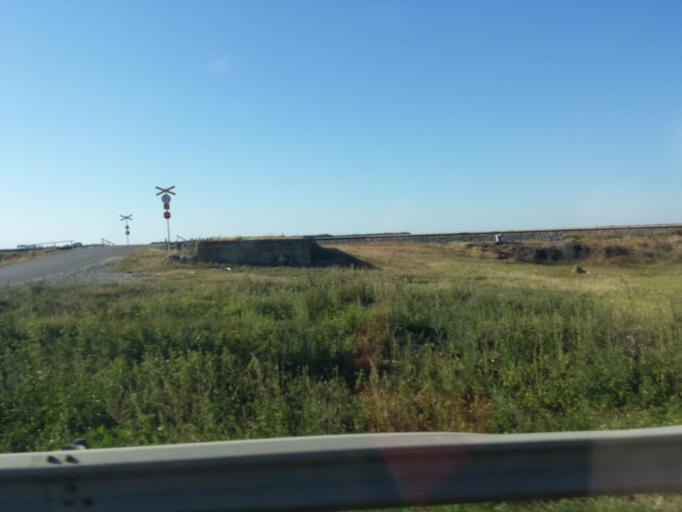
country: RO
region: Ialomita
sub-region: Comuna Cosambesti
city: Cosambesti
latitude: 44.5907
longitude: 27.4468
